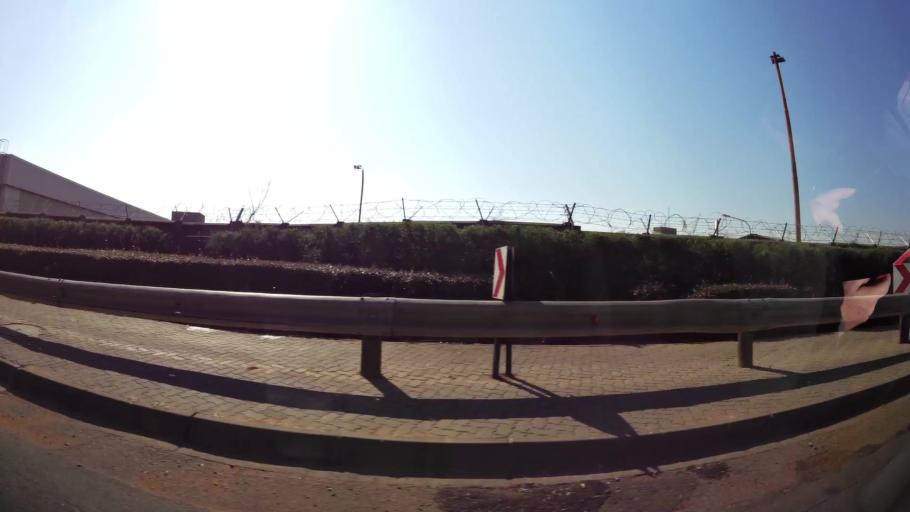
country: ZA
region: Gauteng
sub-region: City of Johannesburg Metropolitan Municipality
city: Modderfontein
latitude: -26.1423
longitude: 28.2230
